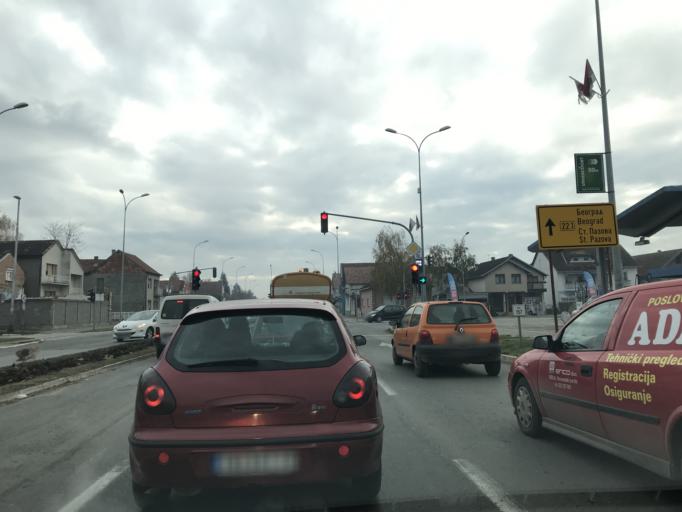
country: RS
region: Autonomna Pokrajina Vojvodina
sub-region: Sremski Okrug
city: Ingija
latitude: 45.0414
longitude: 20.0875
